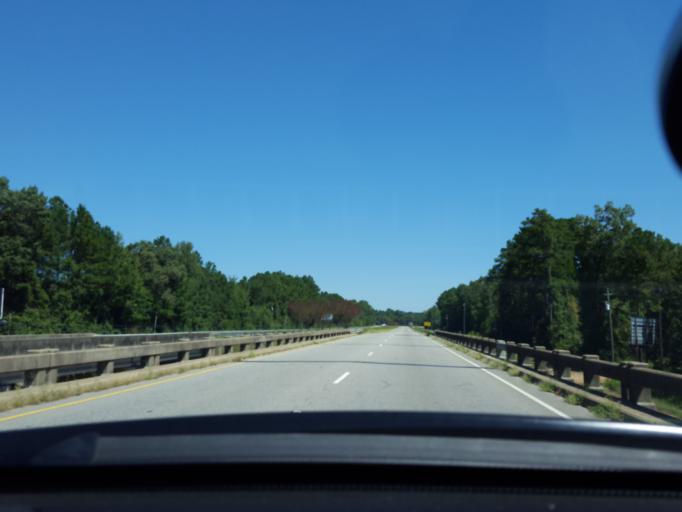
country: US
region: North Carolina
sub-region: Bladen County
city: Elizabethtown
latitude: 34.6375
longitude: -78.5988
